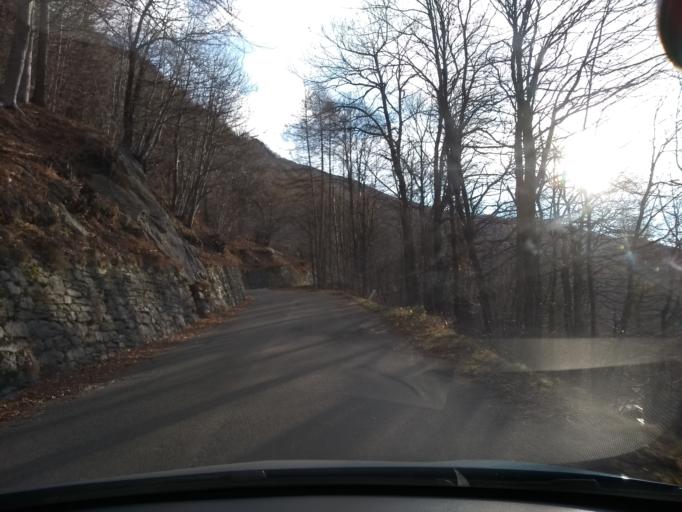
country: IT
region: Piedmont
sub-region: Provincia di Torino
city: Cantoira
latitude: 45.3464
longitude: 7.3795
